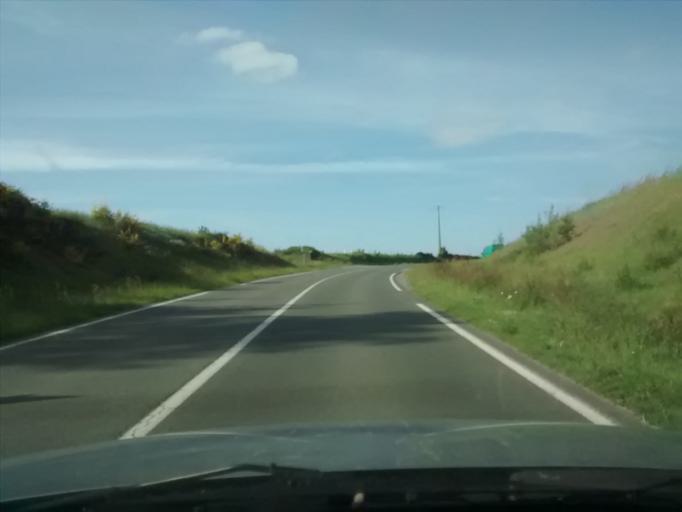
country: FR
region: Pays de la Loire
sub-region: Departement de la Mayenne
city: Entrammes
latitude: 47.9221
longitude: -0.6885
